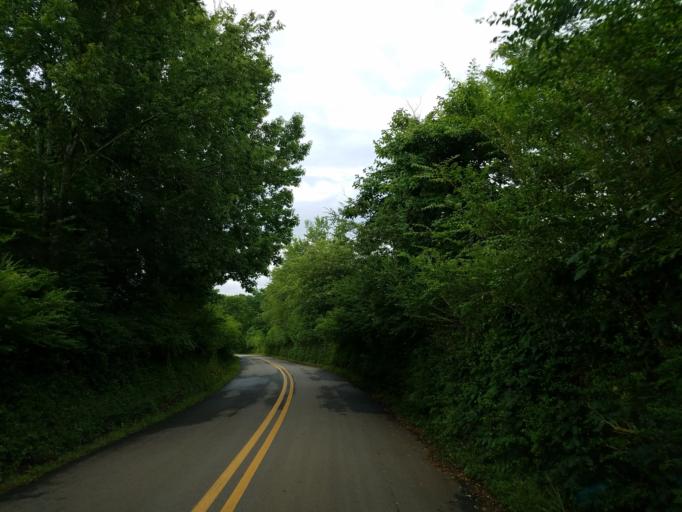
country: US
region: Georgia
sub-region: Pickens County
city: Jasper
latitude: 34.5392
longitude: -84.5329
